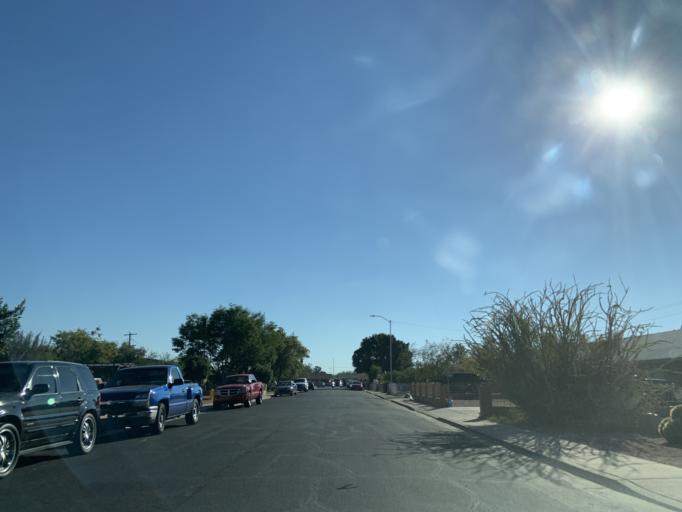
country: US
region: Arizona
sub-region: Maricopa County
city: Mesa
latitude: 33.4059
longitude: -111.8621
